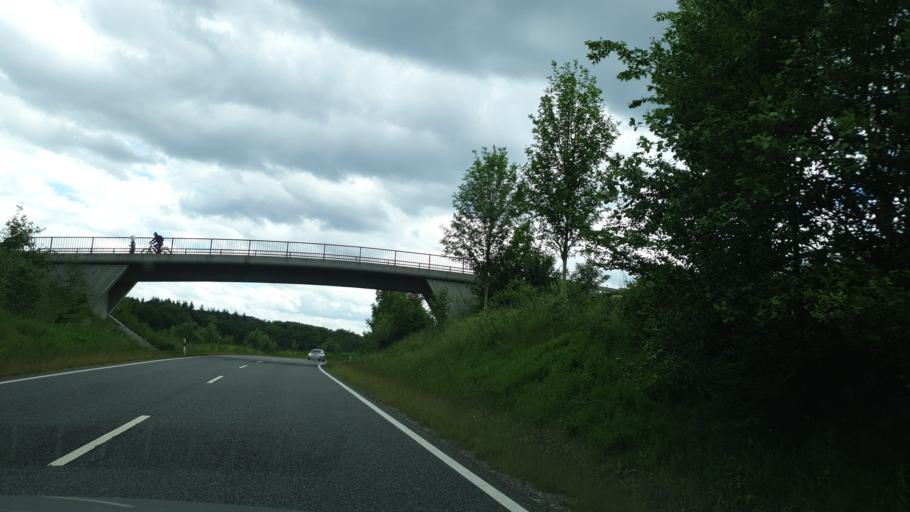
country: DE
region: Rheinland-Pfalz
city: Hohr-Grenzhausen
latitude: 50.4282
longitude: 7.6852
